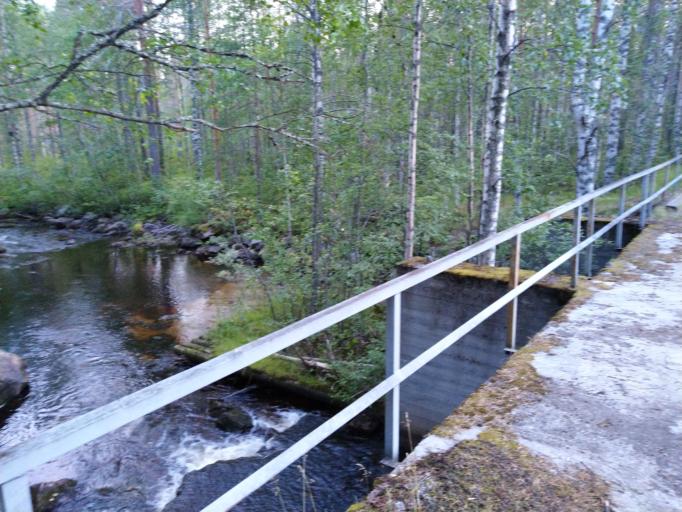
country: FI
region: North Karelia
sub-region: Joensuu
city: Ilomantsi
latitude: 63.1313
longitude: 30.7949
